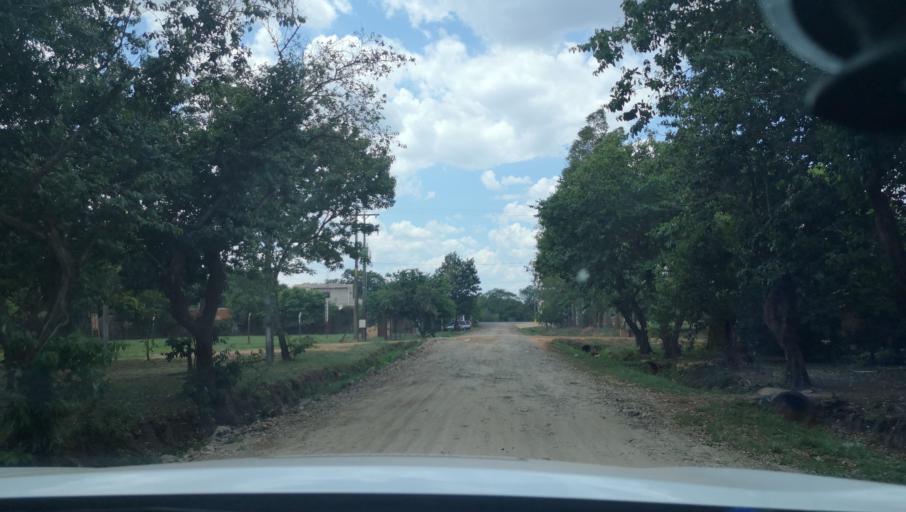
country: PY
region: Itapua
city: Carmen del Parana
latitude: -27.1682
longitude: -56.2316
